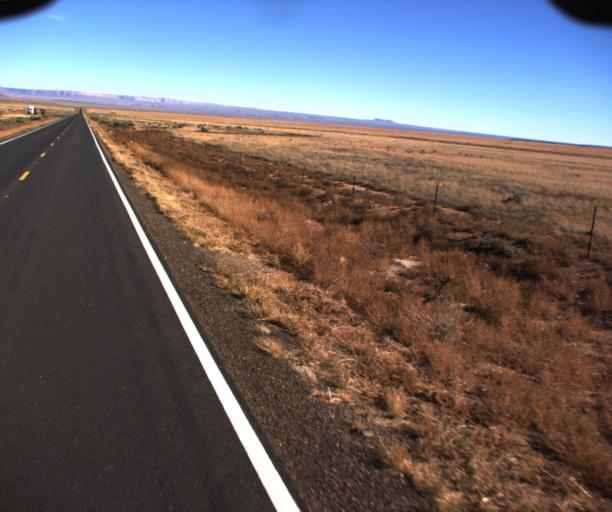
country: US
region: Arizona
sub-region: Coconino County
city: Fredonia
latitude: 36.7301
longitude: -112.0424
